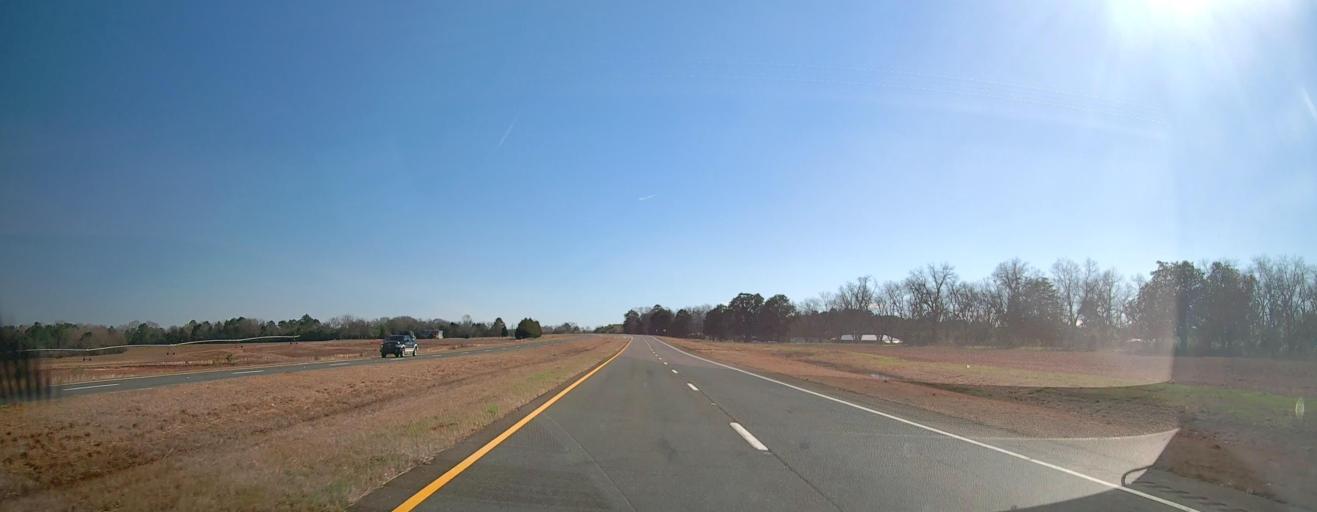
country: US
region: Georgia
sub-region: Sumter County
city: Americus
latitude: 32.1333
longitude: -84.2656
